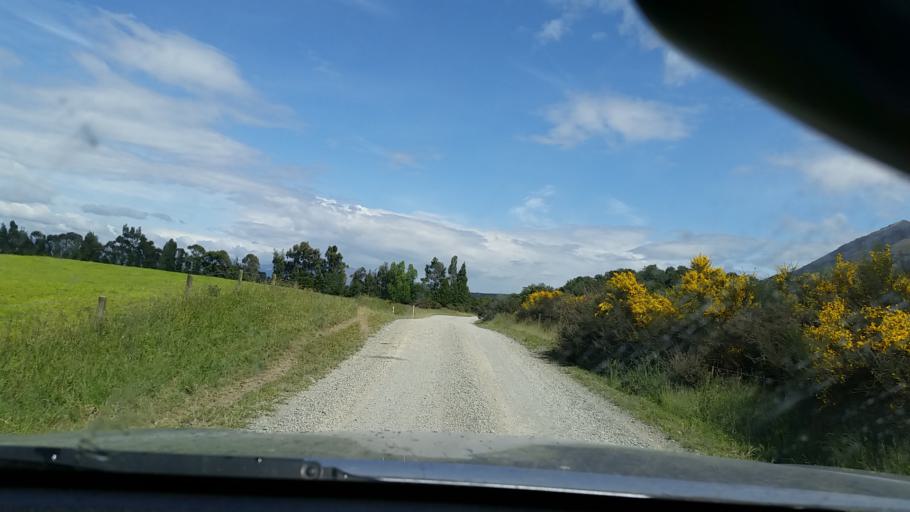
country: NZ
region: Otago
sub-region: Queenstown-Lakes District
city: Kingston
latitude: -45.6252
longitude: 168.2803
